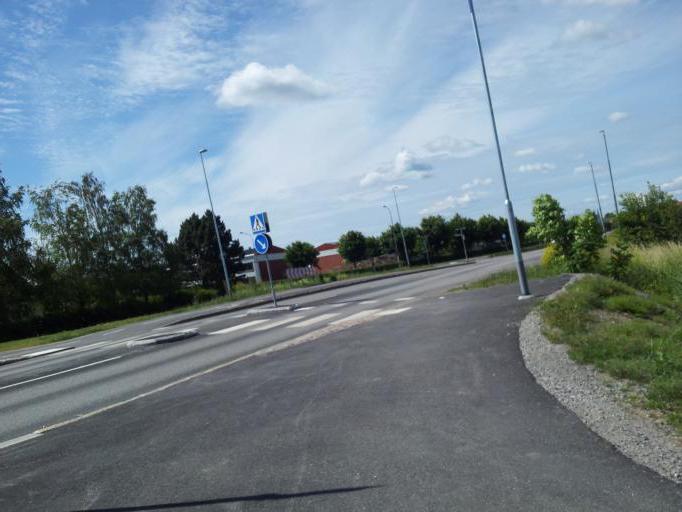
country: SE
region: Uppsala
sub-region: Uppsala Kommun
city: Uppsala
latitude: 59.8741
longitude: 17.6881
